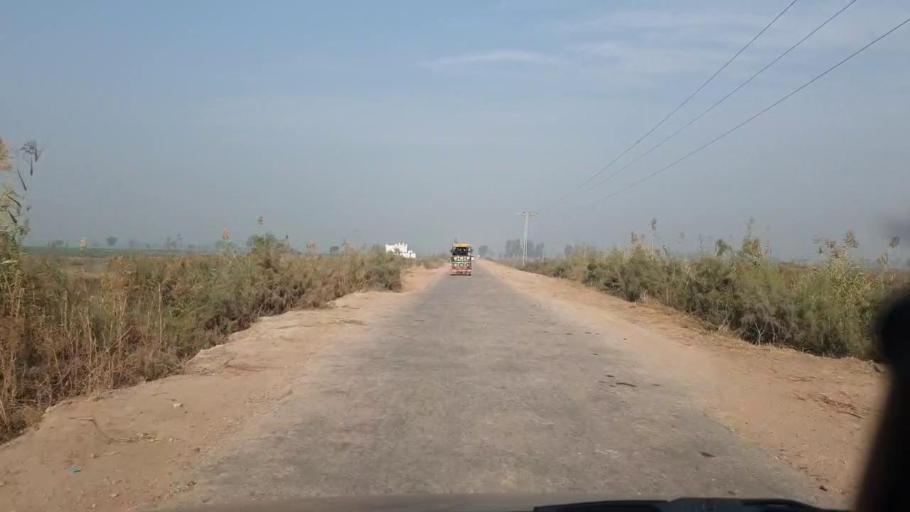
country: PK
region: Sindh
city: Shahdadpur
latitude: 25.9551
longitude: 68.5898
